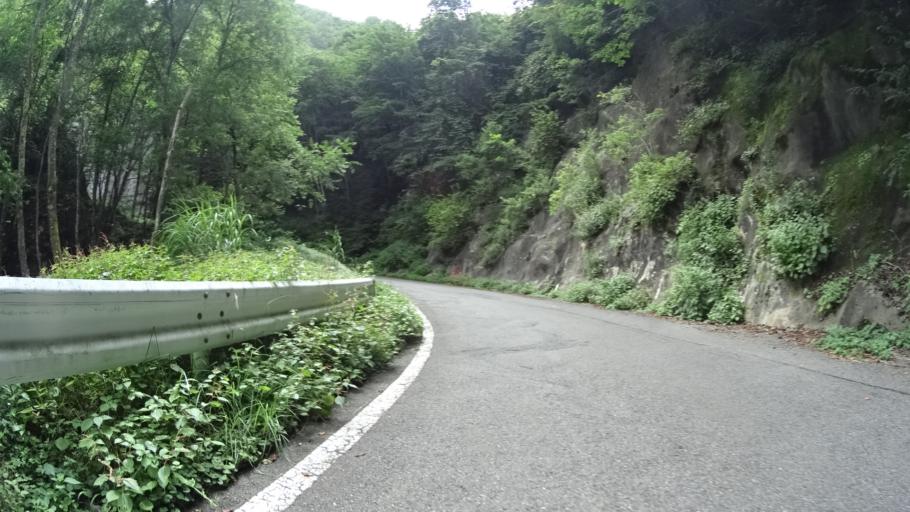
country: JP
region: Nagano
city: Saku
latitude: 36.0685
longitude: 138.6453
